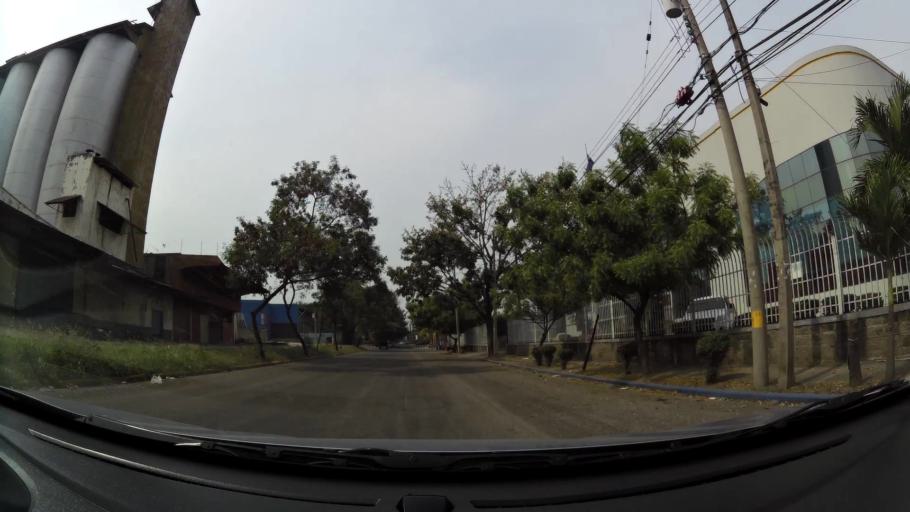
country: HN
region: Cortes
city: San Pedro Sula
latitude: 15.4929
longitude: -88.0250
